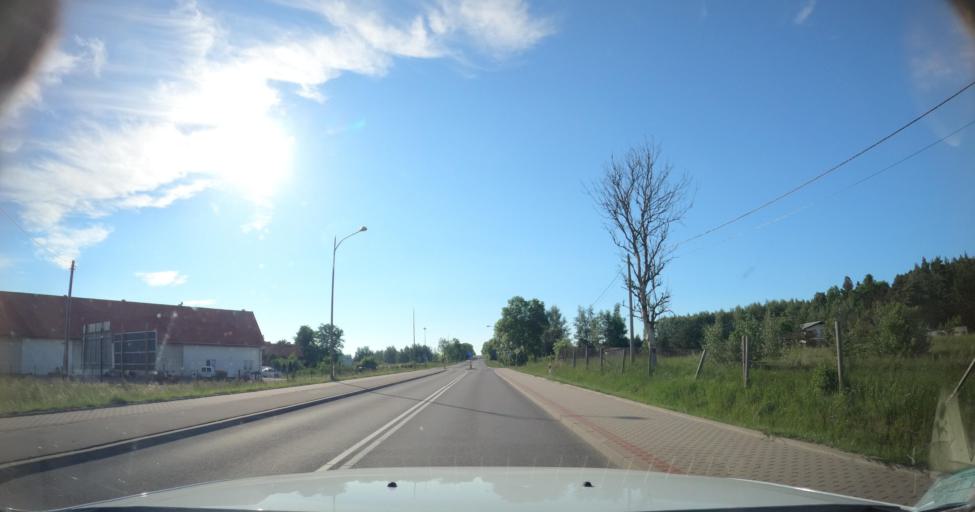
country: PL
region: Warmian-Masurian Voivodeship
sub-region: Powiat elblaski
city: Paslek
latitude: 54.0736
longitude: 19.6397
